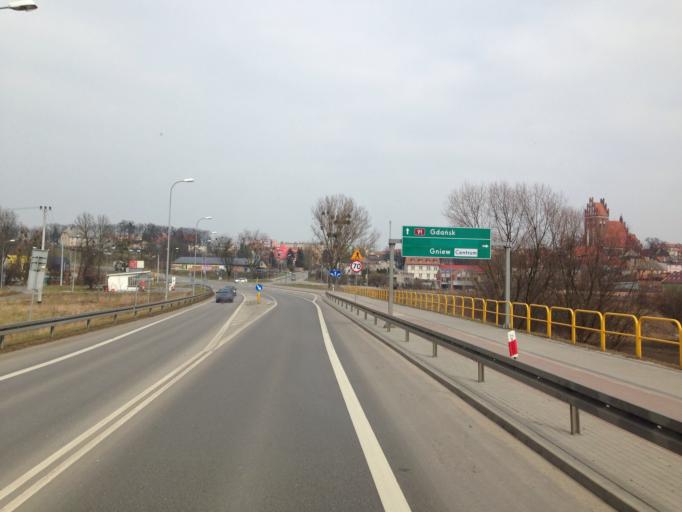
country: PL
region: Pomeranian Voivodeship
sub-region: Powiat tczewski
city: Gniew
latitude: 53.8314
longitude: 18.8185
